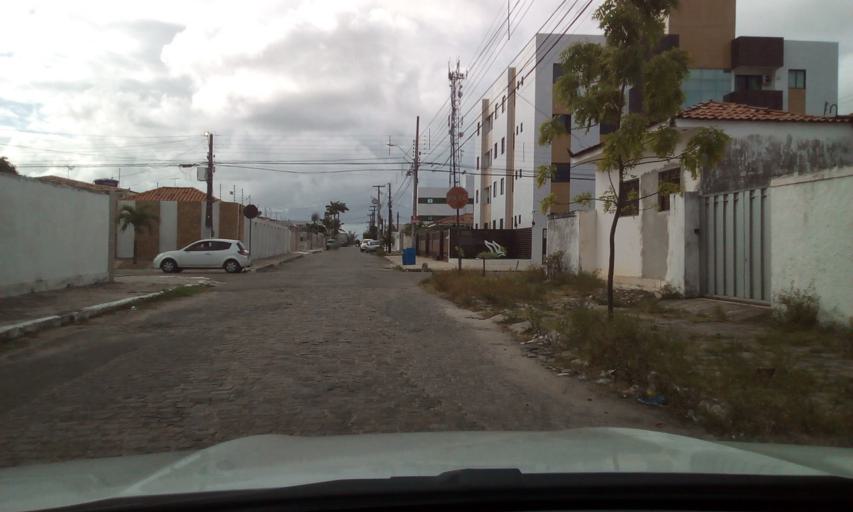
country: BR
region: Paraiba
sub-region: Joao Pessoa
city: Joao Pessoa
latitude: -7.1639
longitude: -34.8705
